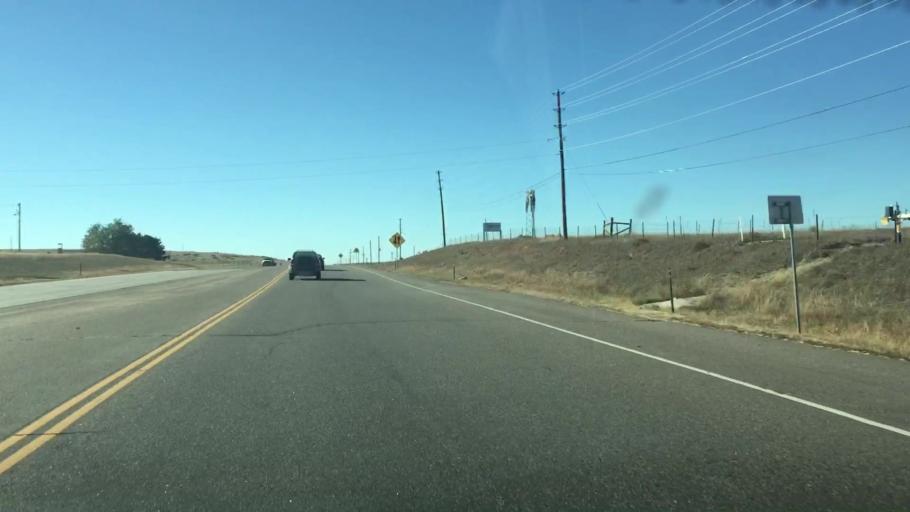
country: US
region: Colorado
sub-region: Douglas County
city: The Pinery
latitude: 39.4317
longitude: -104.7604
